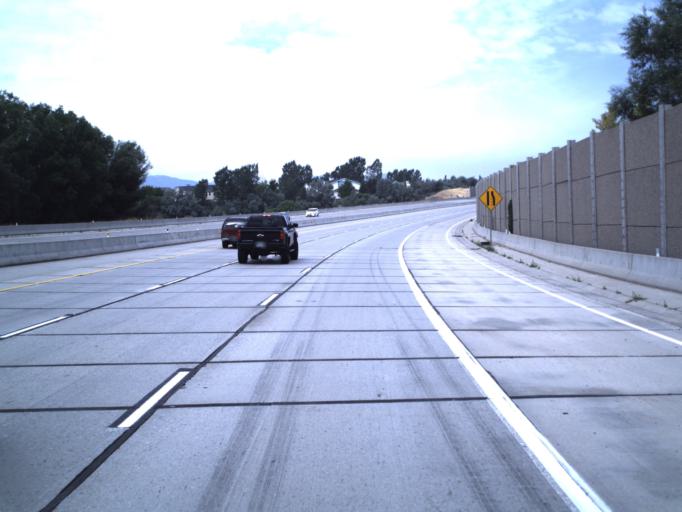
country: US
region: Utah
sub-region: Salt Lake County
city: Bluffdale
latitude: 40.4969
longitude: -111.9256
